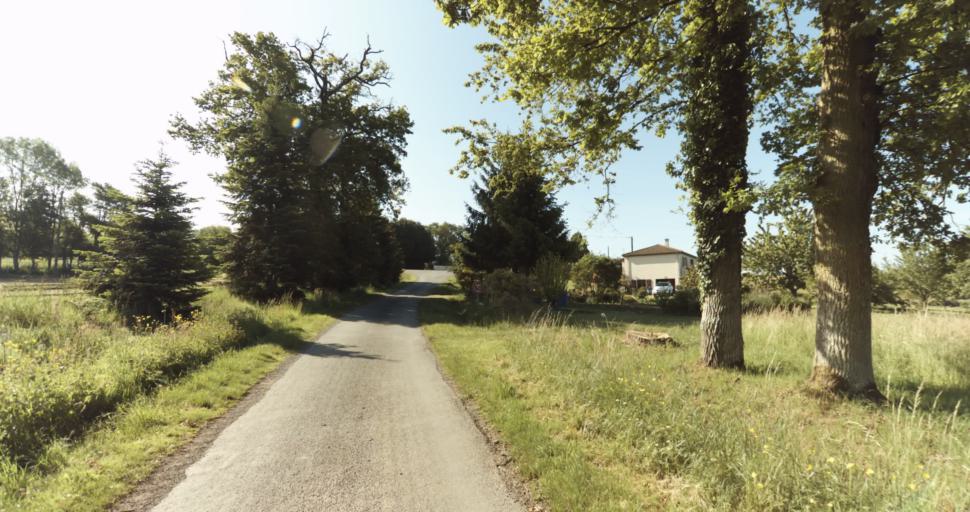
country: FR
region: Limousin
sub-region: Departement de la Haute-Vienne
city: Bosmie-l'Aiguille
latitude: 45.7260
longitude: 1.2381
